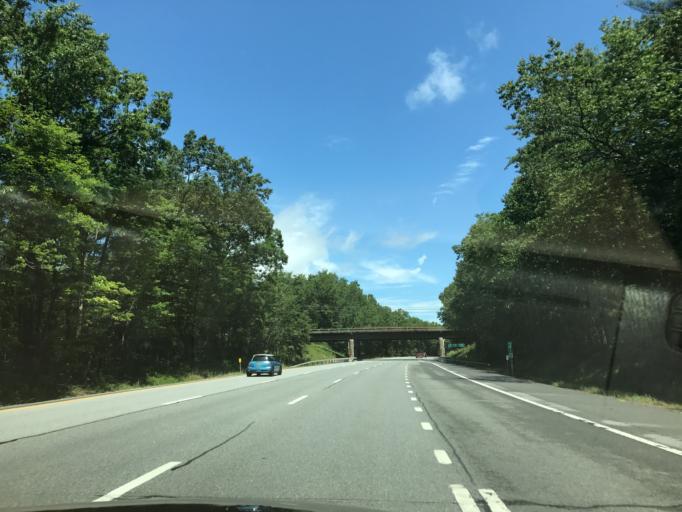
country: US
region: New York
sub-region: Warren County
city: West Glens Falls
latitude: 43.2410
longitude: -73.6917
